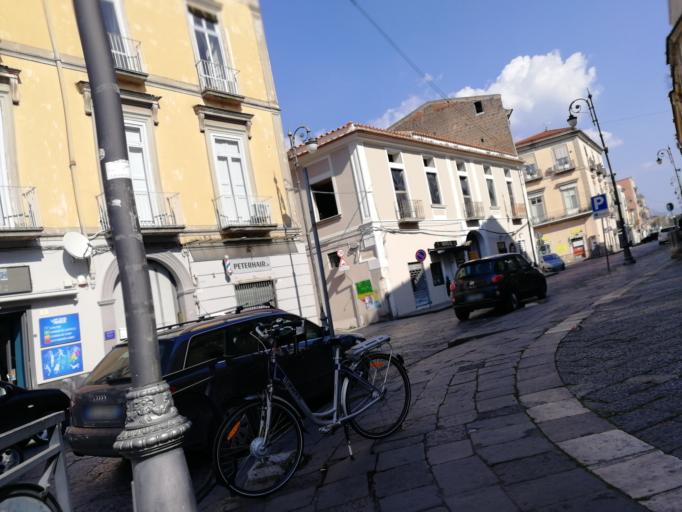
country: IT
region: Campania
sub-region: Provincia di Caserta
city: Santa Maria Capua Vetere
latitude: 41.0817
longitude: 14.2595
